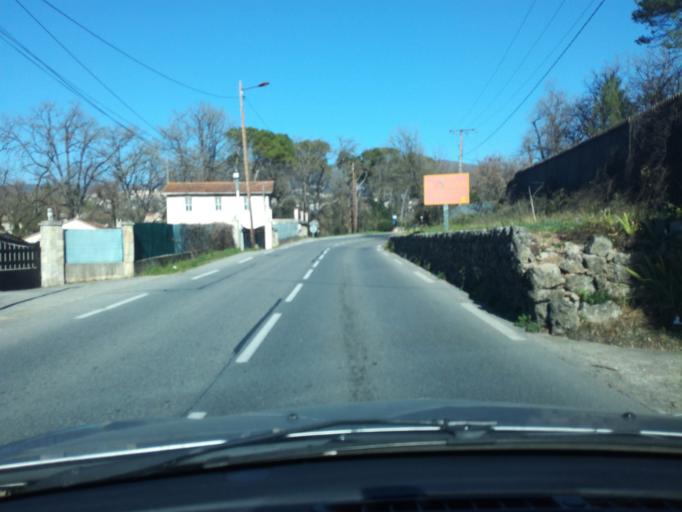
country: FR
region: Provence-Alpes-Cote d'Azur
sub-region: Departement des Alpes-Maritimes
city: Pegomas
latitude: 43.6321
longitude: 6.9319
